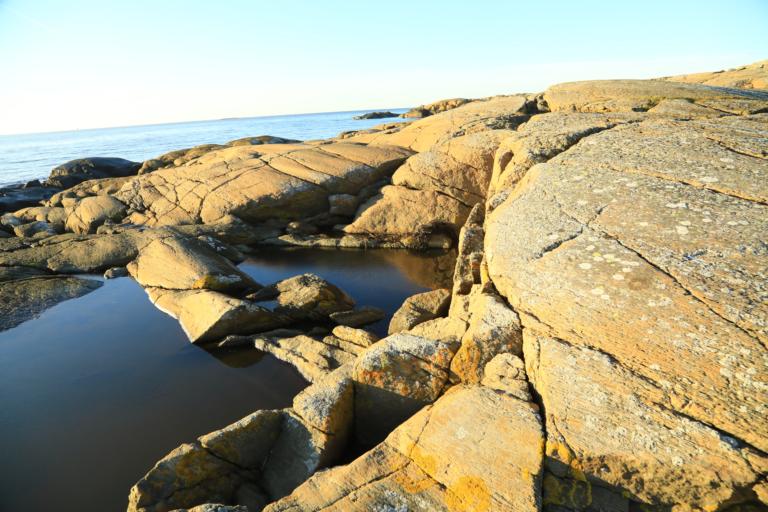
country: SE
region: Halland
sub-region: Varbergs Kommun
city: Varberg
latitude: 57.1878
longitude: 12.1565
